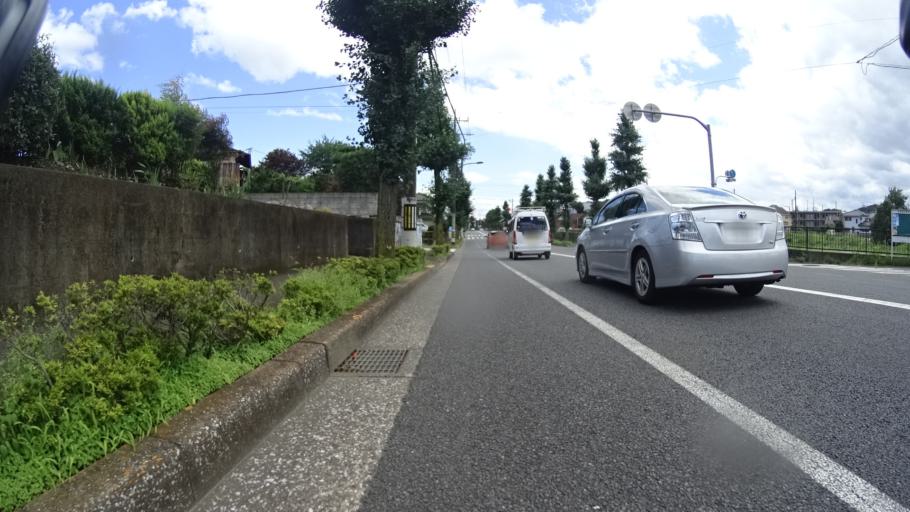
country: JP
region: Tokyo
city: Fussa
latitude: 35.7560
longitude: 139.3147
